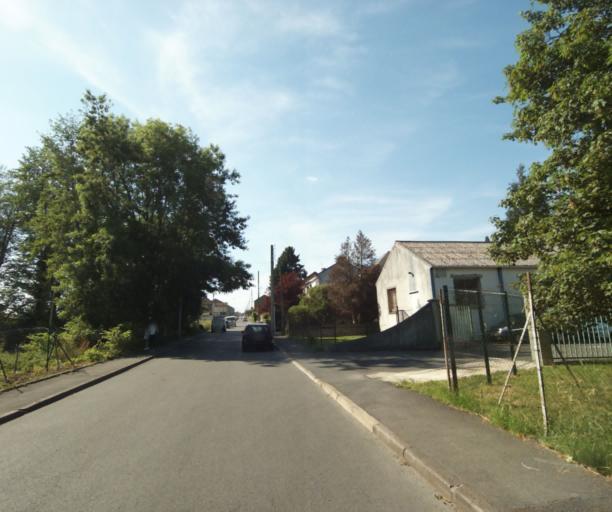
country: FR
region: Champagne-Ardenne
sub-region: Departement des Ardennes
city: Warcq
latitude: 49.7824
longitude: 4.7014
